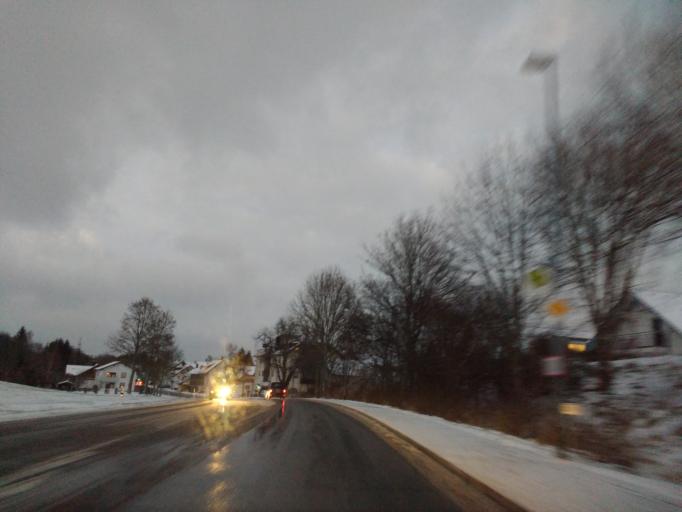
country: DE
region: Bavaria
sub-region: Swabia
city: Buchenberg
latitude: 47.7076
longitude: 10.2741
